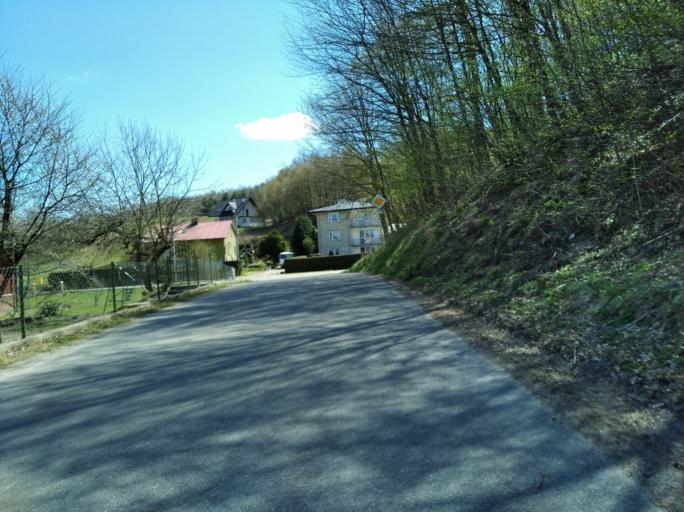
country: PL
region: Subcarpathian Voivodeship
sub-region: Powiat brzozowski
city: Dydnia
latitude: 49.6897
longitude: 22.2138
